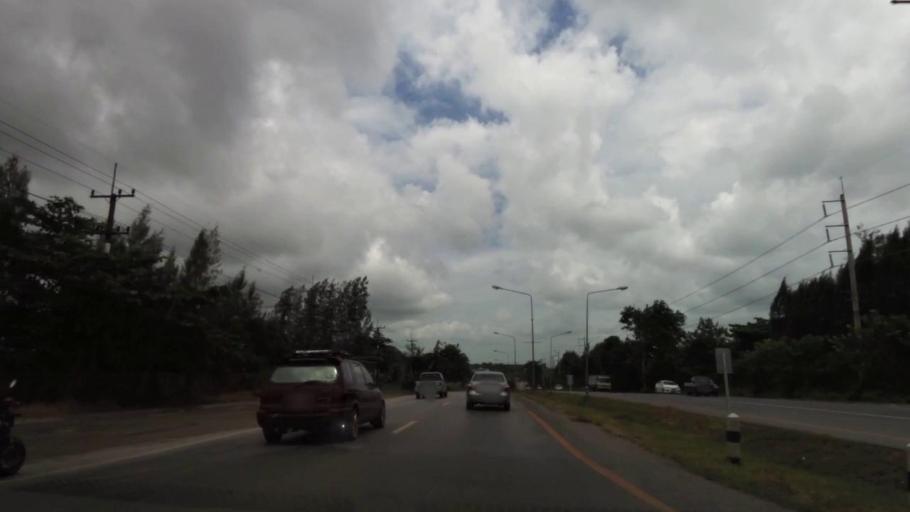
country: TH
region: Chanthaburi
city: Na Yai Am
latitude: 12.7827
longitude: 101.8019
